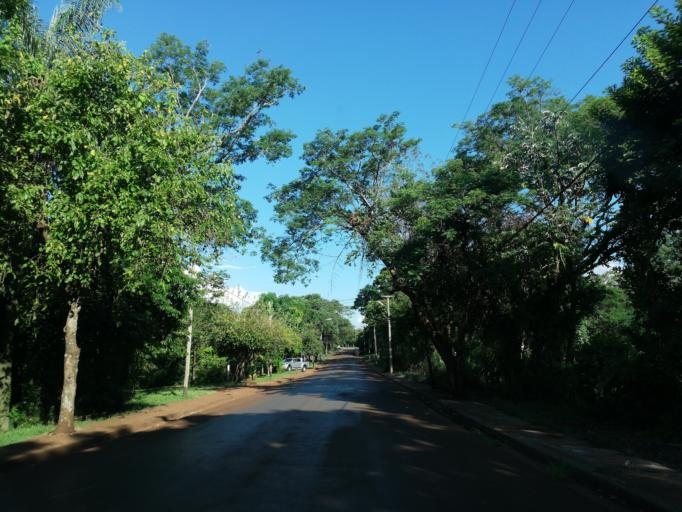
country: AR
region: Misiones
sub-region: Departamento de Capital
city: Posadas
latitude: -27.4037
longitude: -55.9251
